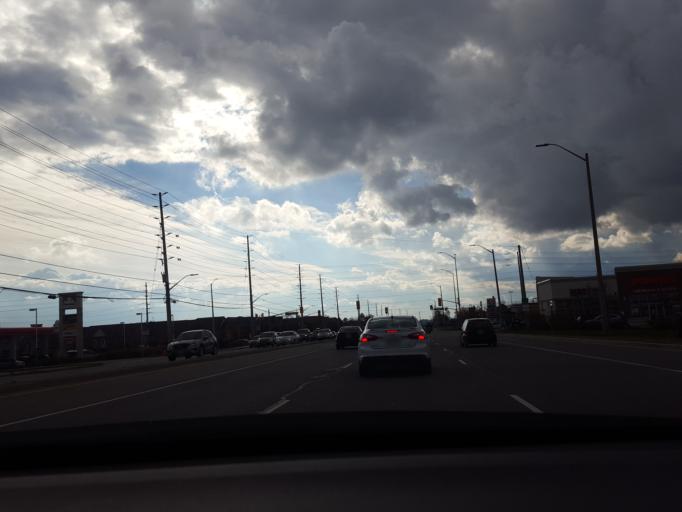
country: CA
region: Ontario
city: Brampton
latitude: 43.6376
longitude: -79.7158
